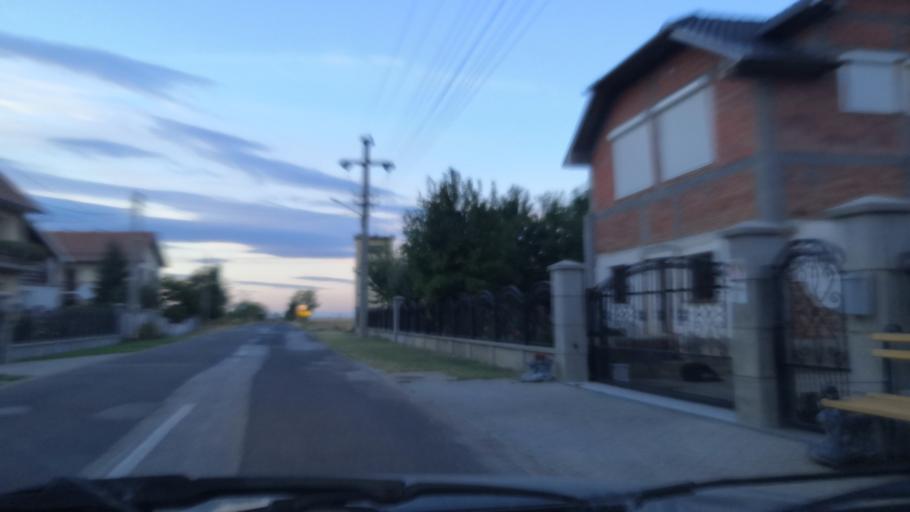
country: RS
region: Central Serbia
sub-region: Borski Okrug
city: Negotin
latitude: 44.2722
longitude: 22.5555
